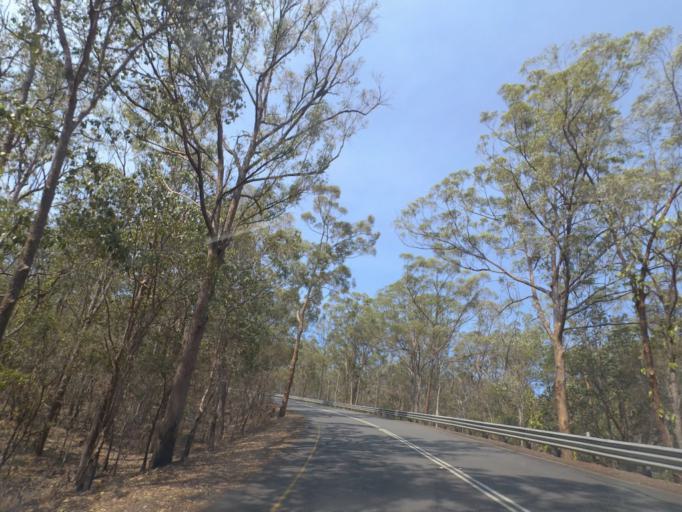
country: AU
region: Queensland
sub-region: Brisbane
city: Robertson
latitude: -27.5577
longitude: 153.0523
